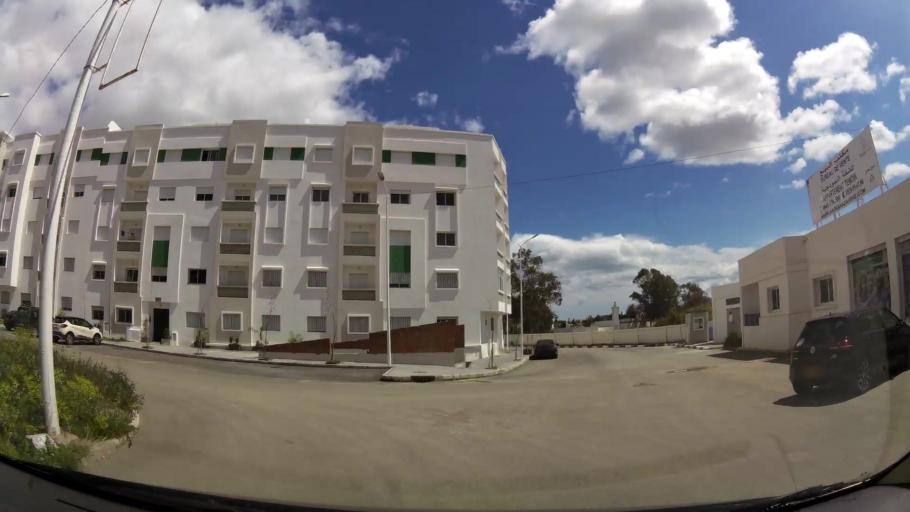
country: MA
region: Tanger-Tetouan
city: Tetouan
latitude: 35.5806
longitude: -5.3408
